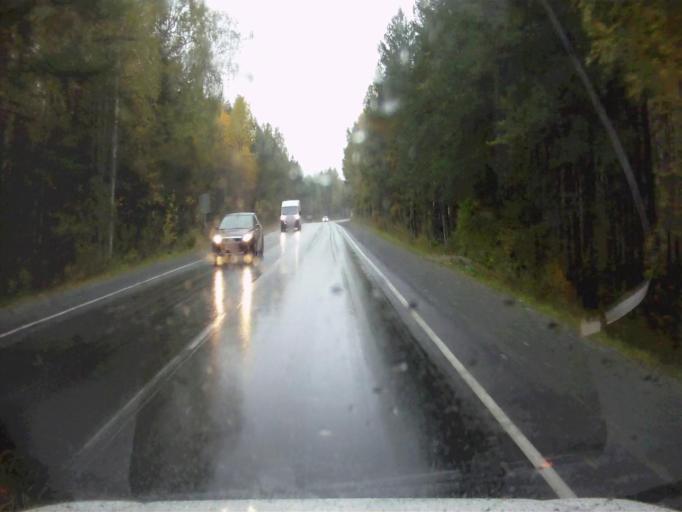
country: RU
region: Chelyabinsk
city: Tayginka
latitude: 55.5946
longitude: 60.6218
